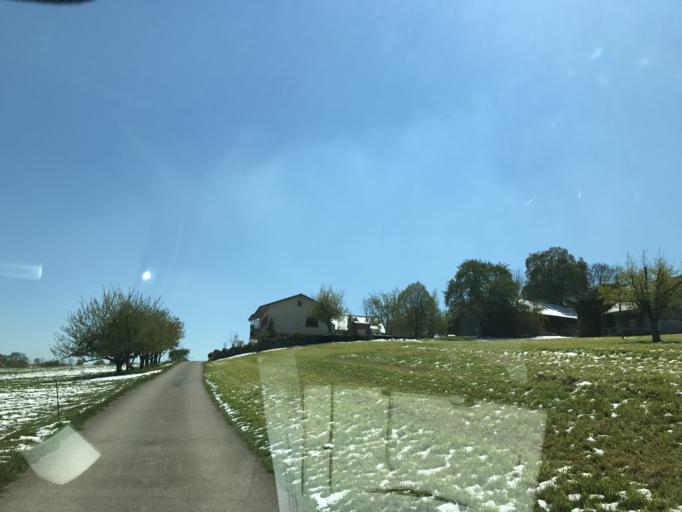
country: CH
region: Lucerne
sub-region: Sursee District
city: Neudorf
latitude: 47.1737
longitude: 8.2104
